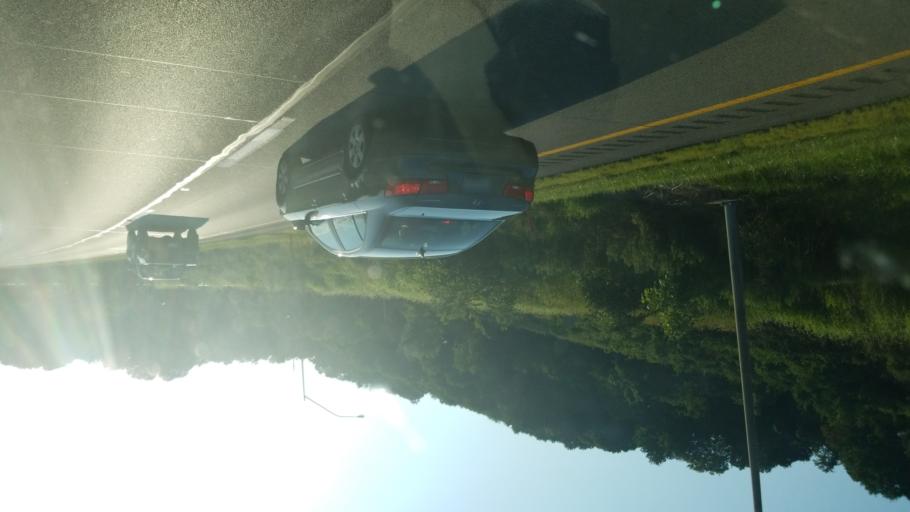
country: US
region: Pennsylvania
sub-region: Allegheny County
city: Coraopolis
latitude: 40.5018
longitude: -80.1341
